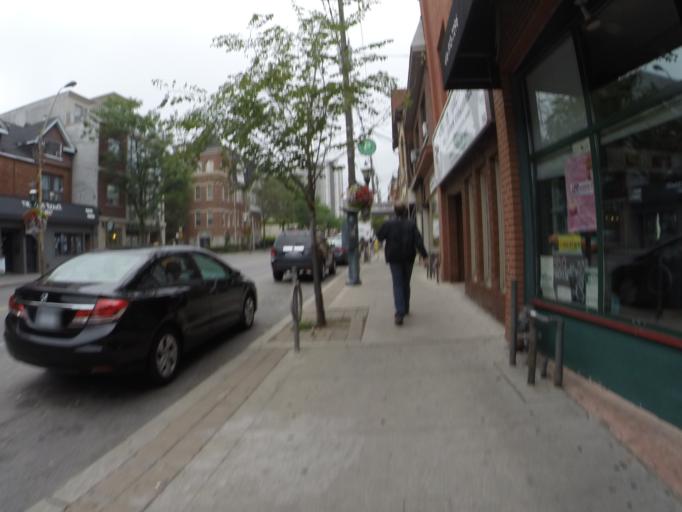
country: CA
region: Ontario
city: Toronto
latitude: 43.6635
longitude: -79.3678
